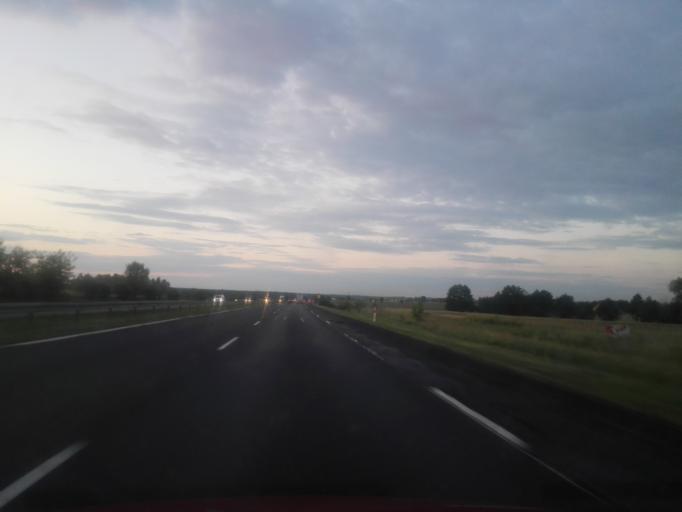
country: PL
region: Lodz Voivodeship
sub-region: Powiat radomszczanski
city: Kamiensk
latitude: 51.2035
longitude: 19.4795
